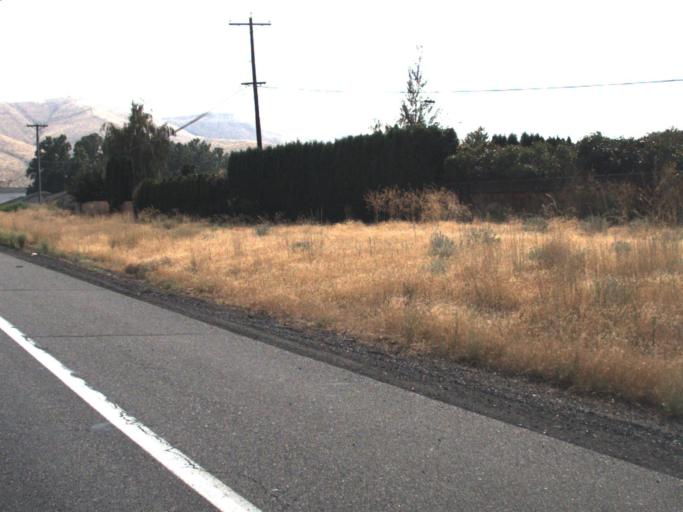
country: US
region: Washington
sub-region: Benton County
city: Prosser
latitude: 46.2118
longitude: -119.7476
